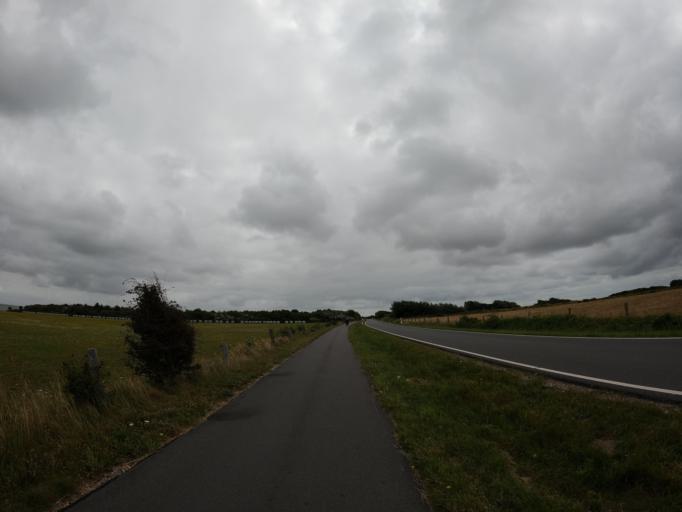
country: DE
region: Schleswig-Holstein
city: Tinnum
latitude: 54.9432
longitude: 8.3481
